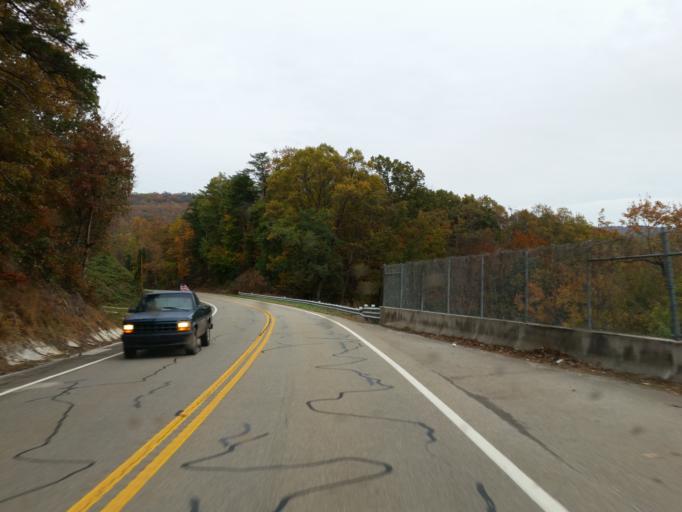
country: US
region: Georgia
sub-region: Pickens County
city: Jasper
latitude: 34.5292
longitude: -84.3950
